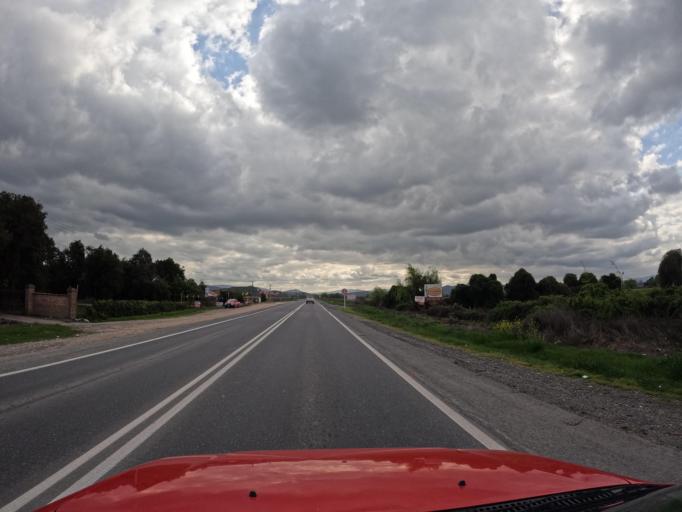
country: CL
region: Maule
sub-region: Provincia de Linares
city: San Javier
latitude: -35.6332
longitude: -71.7091
